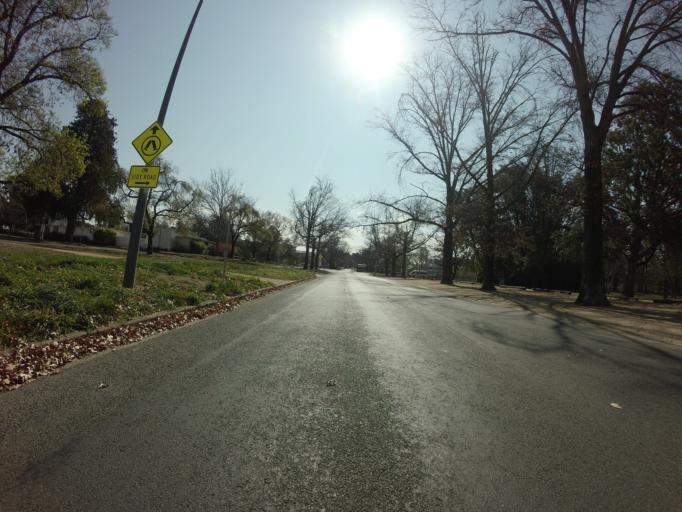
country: AU
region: Australian Capital Territory
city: Forrest
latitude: -35.3165
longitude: 149.1361
